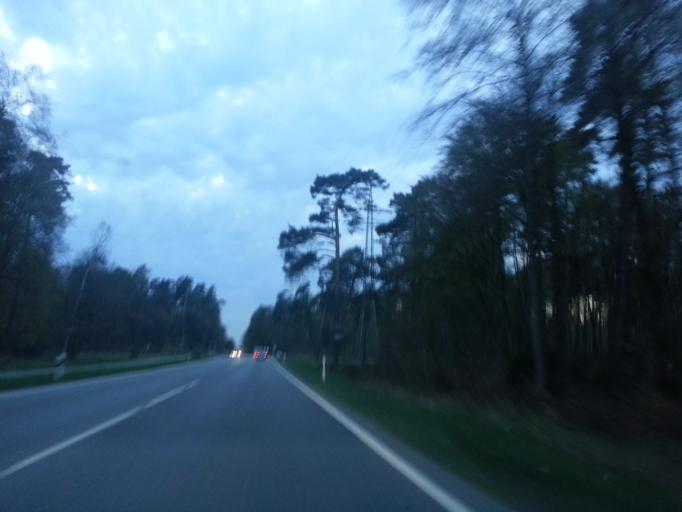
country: DE
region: Baden-Wuerttemberg
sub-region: Tuebingen Region
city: Eriskirch
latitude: 47.6228
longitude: 9.5565
